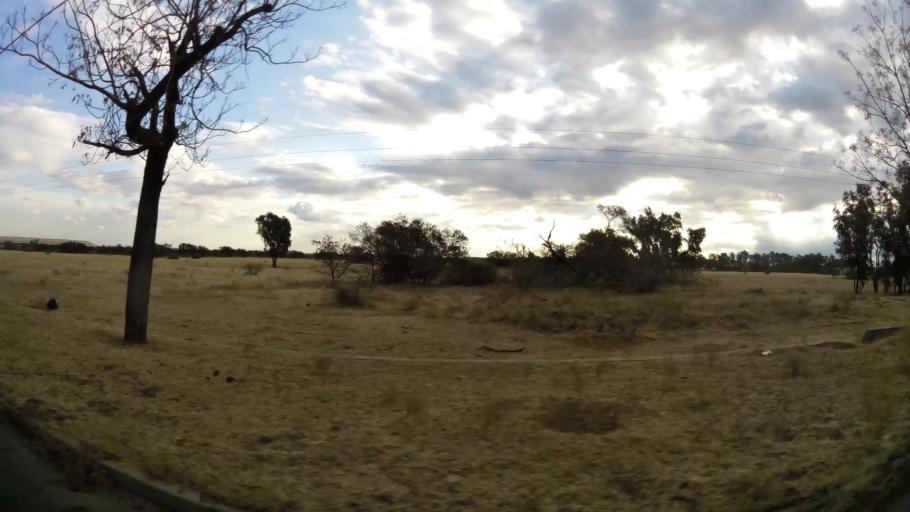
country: ZA
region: Orange Free State
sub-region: Lejweleputswa District Municipality
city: Welkom
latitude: -28.0040
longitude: 26.7101
